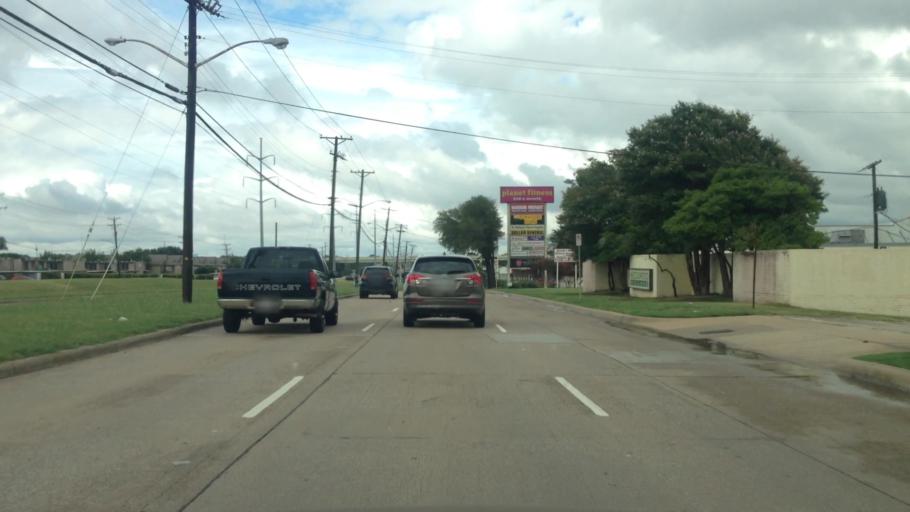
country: US
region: Texas
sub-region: Tarrant County
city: Edgecliff Village
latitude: 32.6712
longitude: -97.3853
